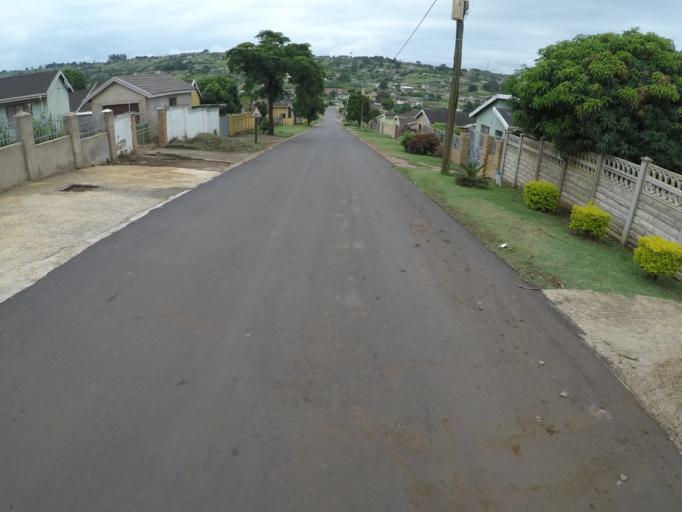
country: ZA
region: KwaZulu-Natal
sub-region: uThungulu District Municipality
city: Empangeni
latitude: -28.7765
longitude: 31.8505
